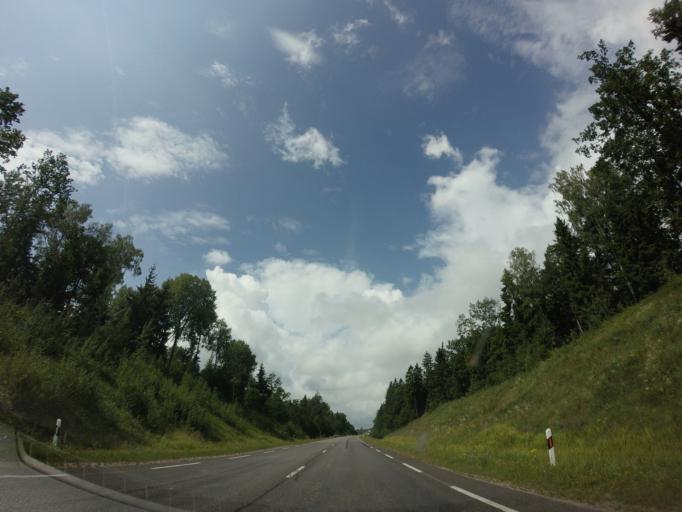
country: LT
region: Alytaus apskritis
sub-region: Alytaus rajonas
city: Daugai
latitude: 54.3582
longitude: 24.2789
